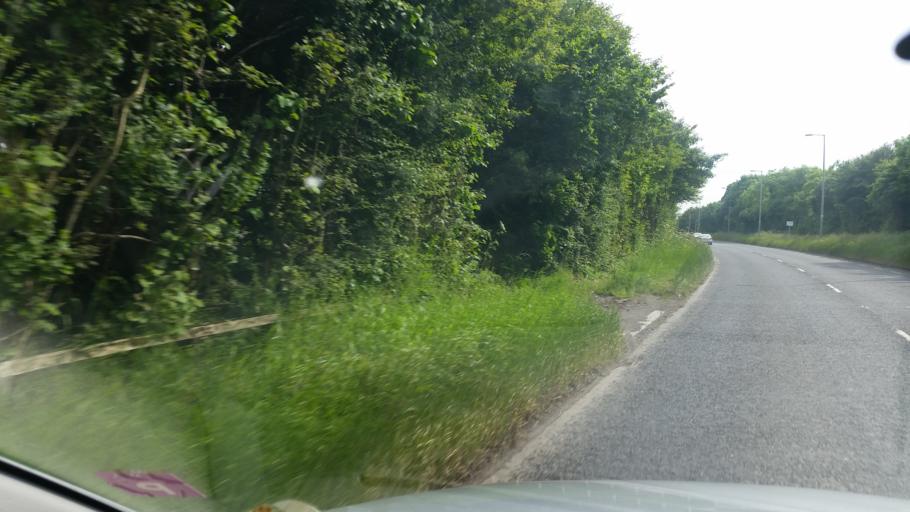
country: IE
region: Leinster
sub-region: Dublin City
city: Finglas
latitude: 53.4276
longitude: -6.3035
